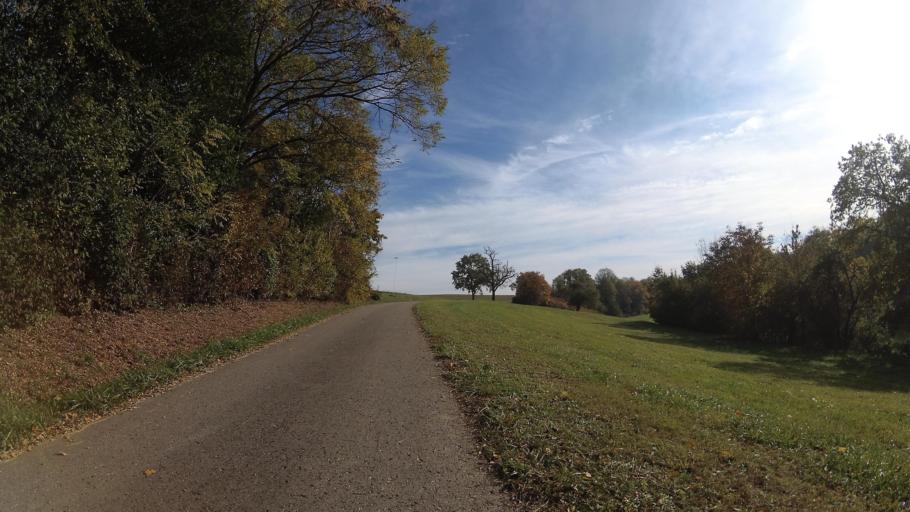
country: DE
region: Baden-Wuerttemberg
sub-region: Regierungsbezirk Stuttgart
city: Neuenstein
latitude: 49.2041
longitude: 9.5475
